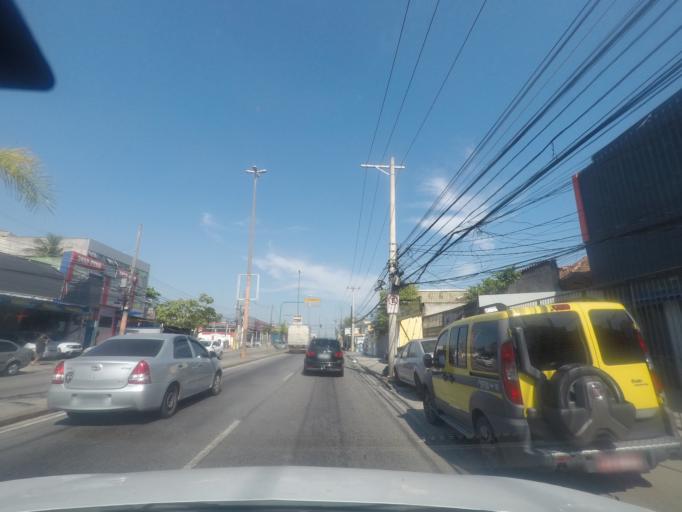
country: BR
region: Rio de Janeiro
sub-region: Sao Joao De Meriti
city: Sao Joao de Meriti
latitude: -22.8774
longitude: -43.3649
